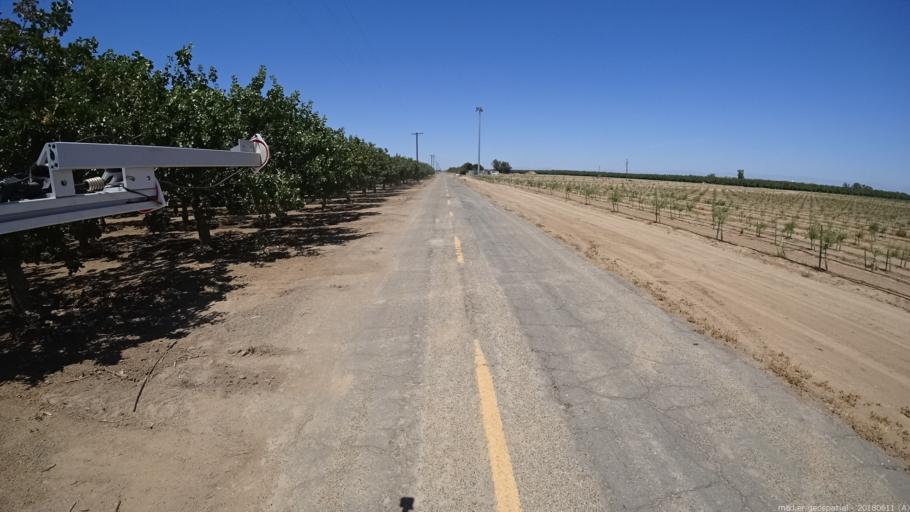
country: US
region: California
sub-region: Madera County
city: Fairmead
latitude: 37.0240
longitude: -120.2114
